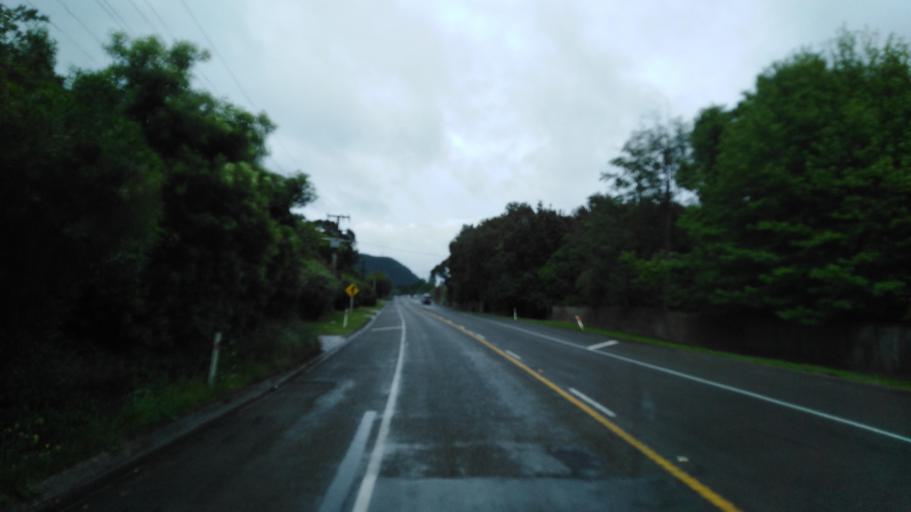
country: NZ
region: Wellington
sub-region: Kapiti Coast District
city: Otaki
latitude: -40.7269
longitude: 175.2089
